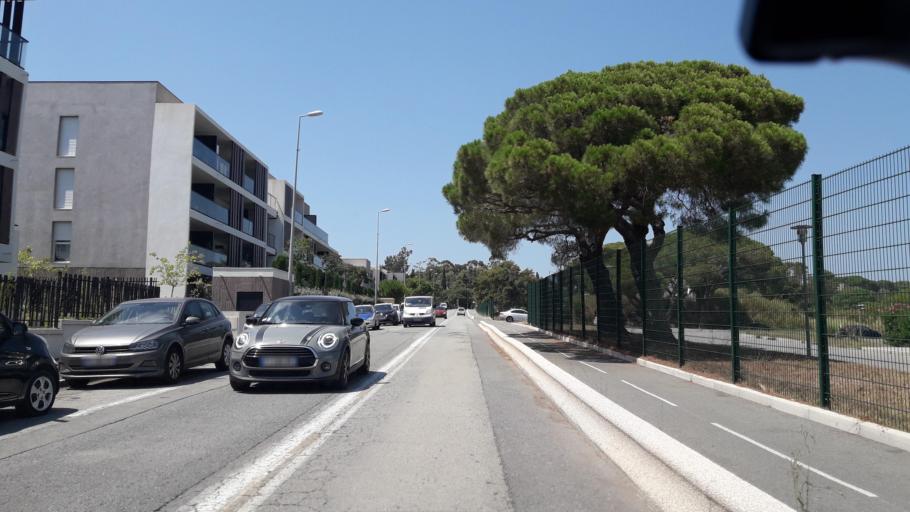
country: FR
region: Provence-Alpes-Cote d'Azur
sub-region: Departement du Var
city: Frejus
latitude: 43.4458
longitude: 6.7546
